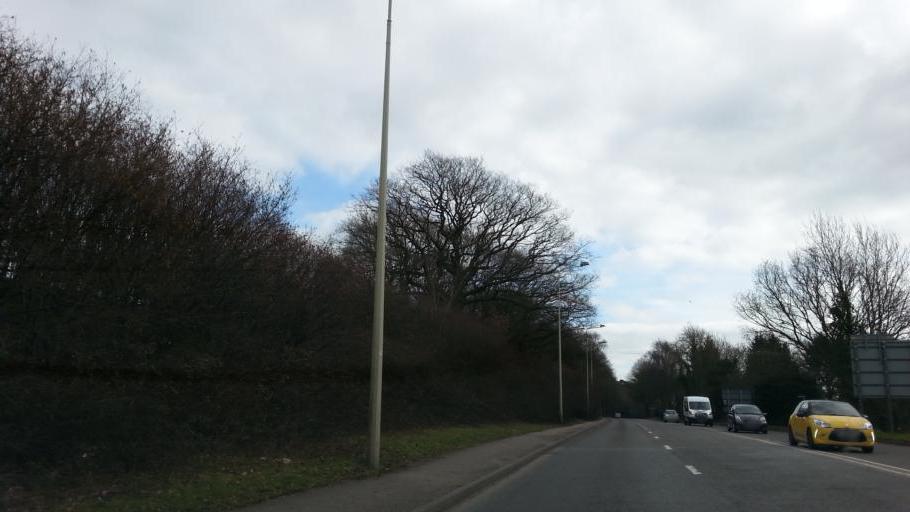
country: GB
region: England
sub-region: Staffordshire
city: Rugeley
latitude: 52.7412
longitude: -1.9139
